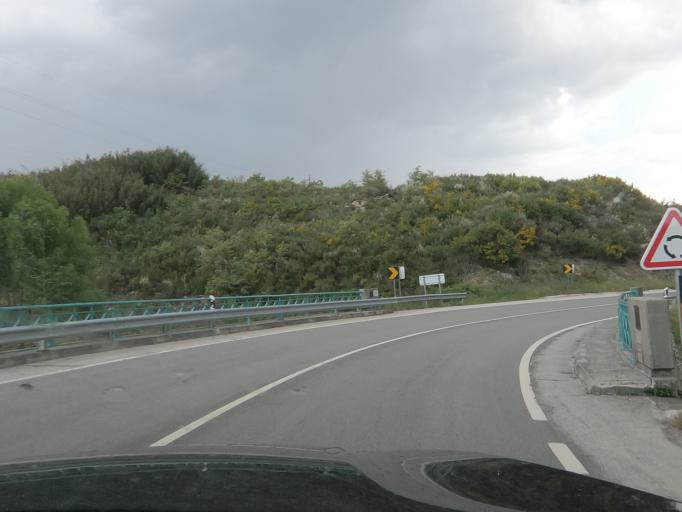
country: PT
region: Vila Real
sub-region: Vila Real
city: Vila Real
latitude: 41.3759
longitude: -7.7187
